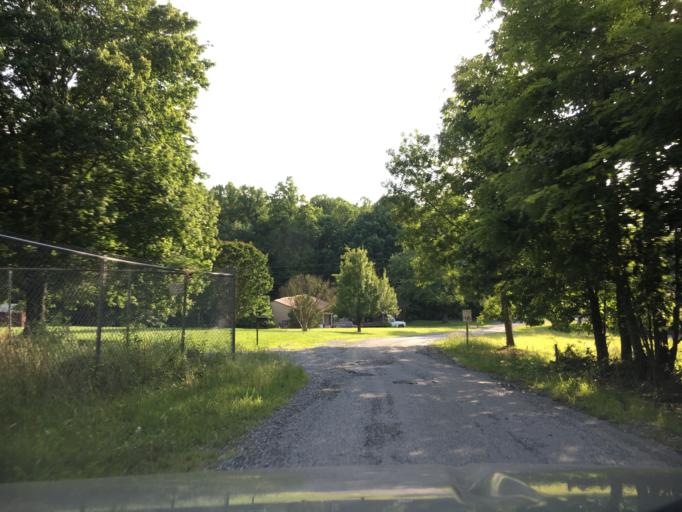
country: US
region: Virginia
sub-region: City of Lynchburg
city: West Lynchburg
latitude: 37.3338
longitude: -79.1848
